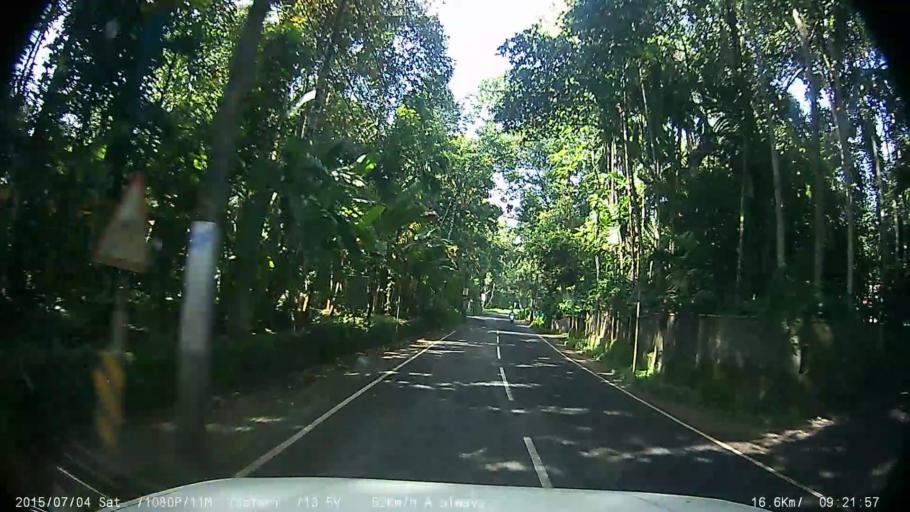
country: IN
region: Kerala
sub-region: Kottayam
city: Palackattumala
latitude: 9.6820
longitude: 76.6116
